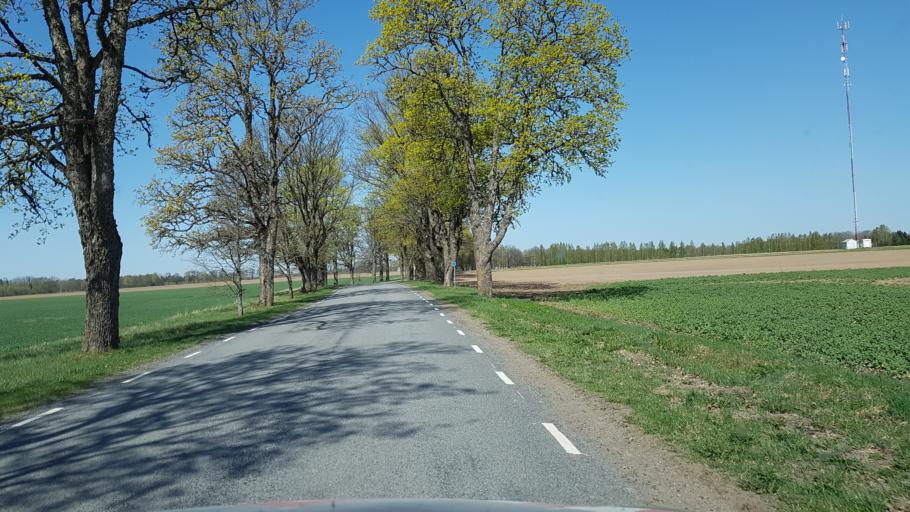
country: EE
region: Viljandimaa
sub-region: Vohma linn
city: Vohma
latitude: 58.5430
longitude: 25.5722
